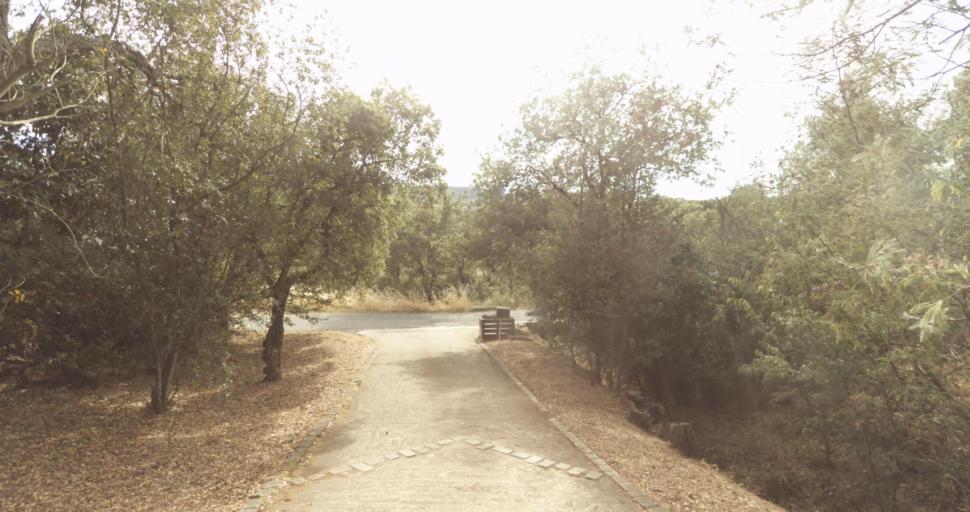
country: FR
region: Provence-Alpes-Cote d'Azur
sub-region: Departement du Var
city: Gassin
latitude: 43.2201
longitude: 6.5812
